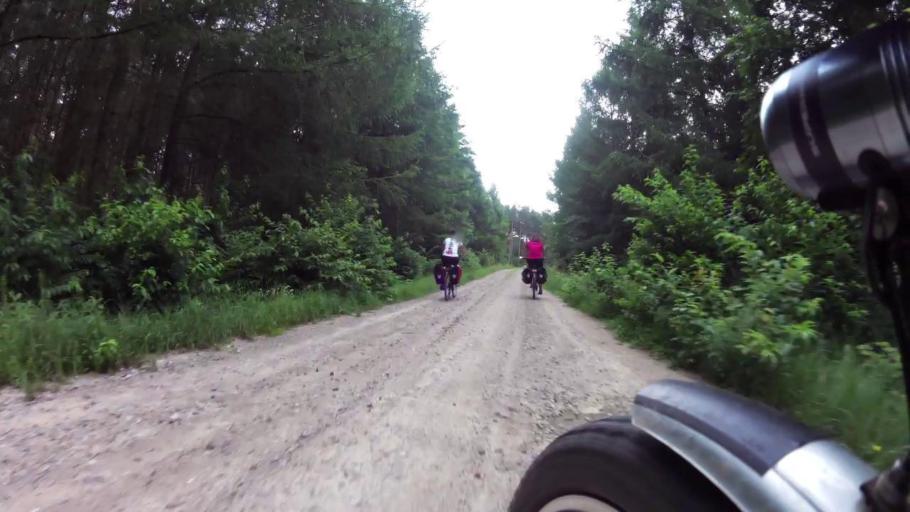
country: PL
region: West Pomeranian Voivodeship
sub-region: Powiat gryfinski
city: Mieszkowice
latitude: 52.8394
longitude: 14.5954
